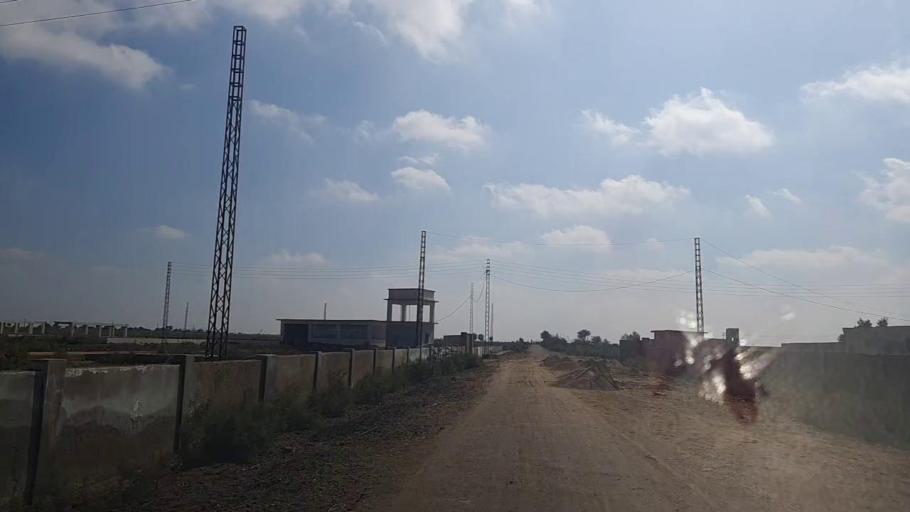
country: PK
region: Sindh
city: Sanghar
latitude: 26.0646
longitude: 69.0046
